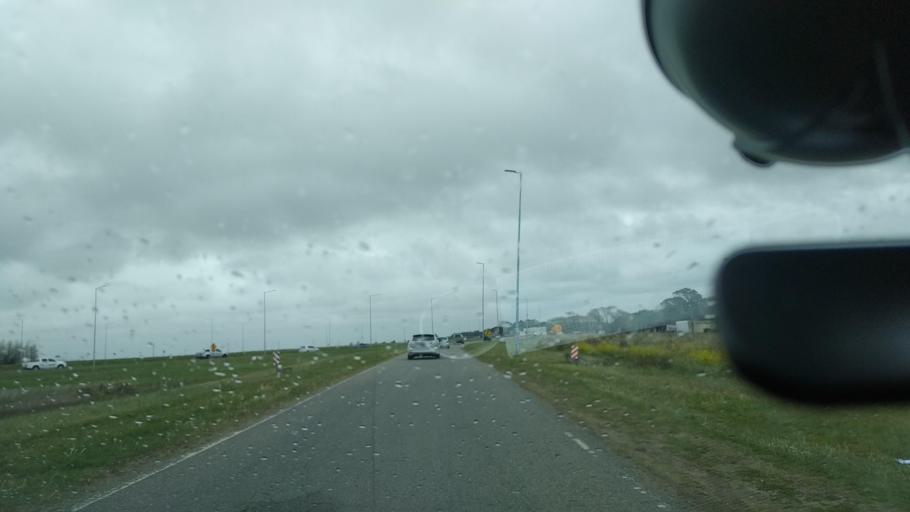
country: AR
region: Buenos Aires
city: San Clemente del Tuyu
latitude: -36.3885
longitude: -56.7392
